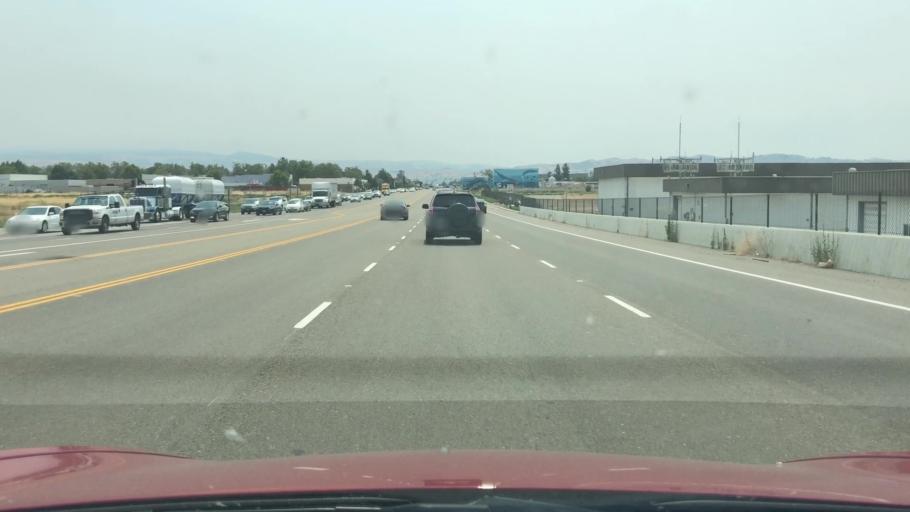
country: US
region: California
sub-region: Alameda County
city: Livermore
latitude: 37.6956
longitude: -121.8057
